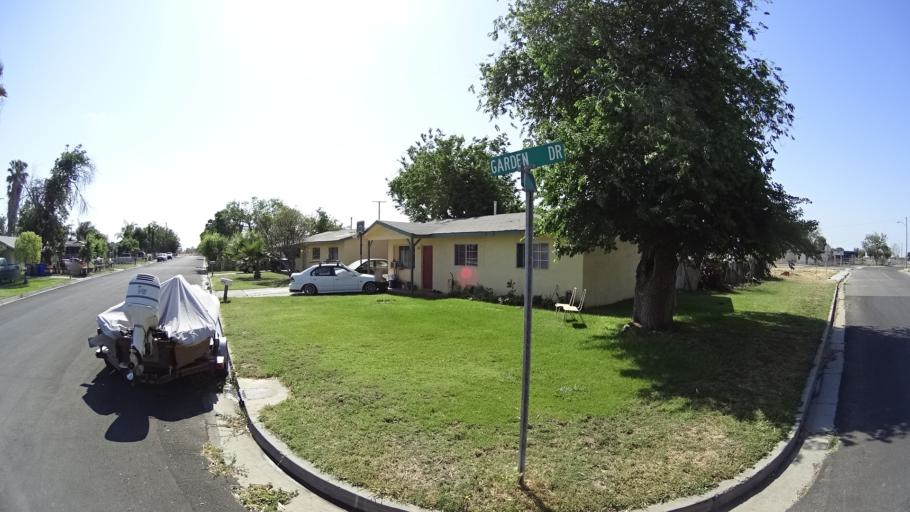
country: US
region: California
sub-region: Kings County
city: Home Garden
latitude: 36.3026
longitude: -119.6309
